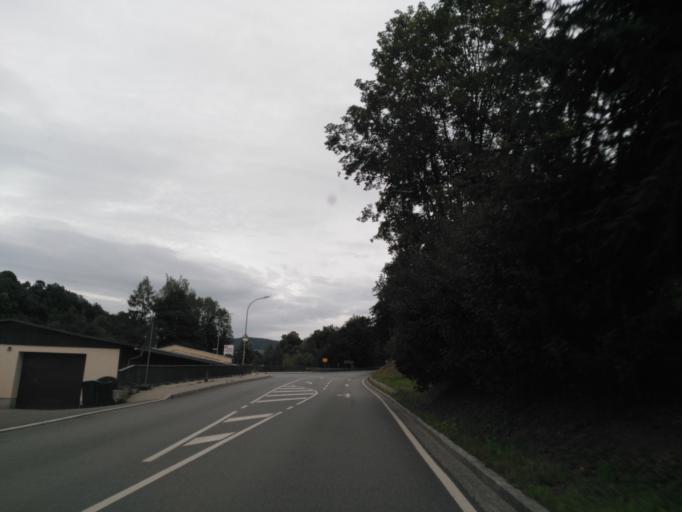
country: DE
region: Saxony
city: Schwarzenberg
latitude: 50.5376
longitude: 12.8000
